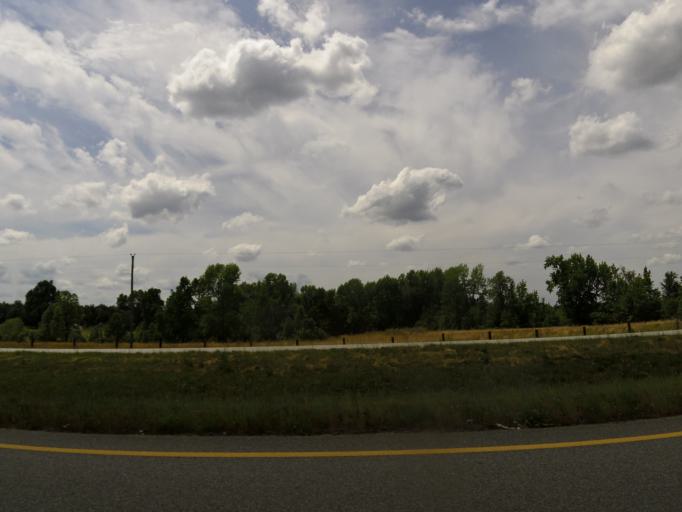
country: US
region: Georgia
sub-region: Jefferson County
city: Wadley
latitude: 32.7435
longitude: -82.3931
